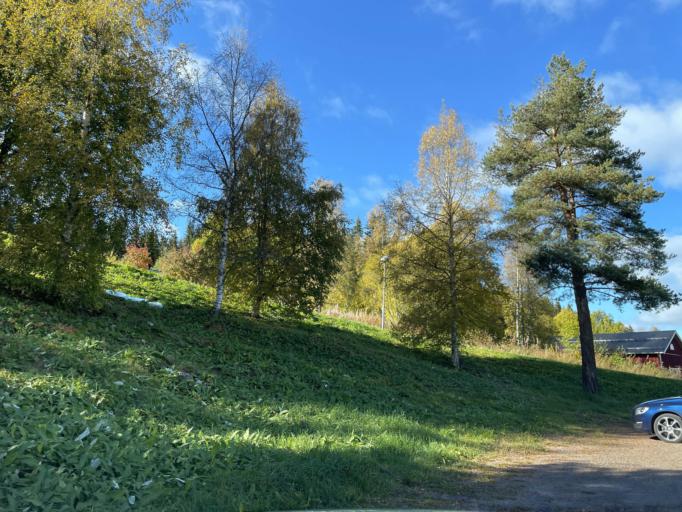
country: SE
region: Dalarna
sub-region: Malung-Saelens kommun
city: Malung
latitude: 61.1581
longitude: 13.2570
